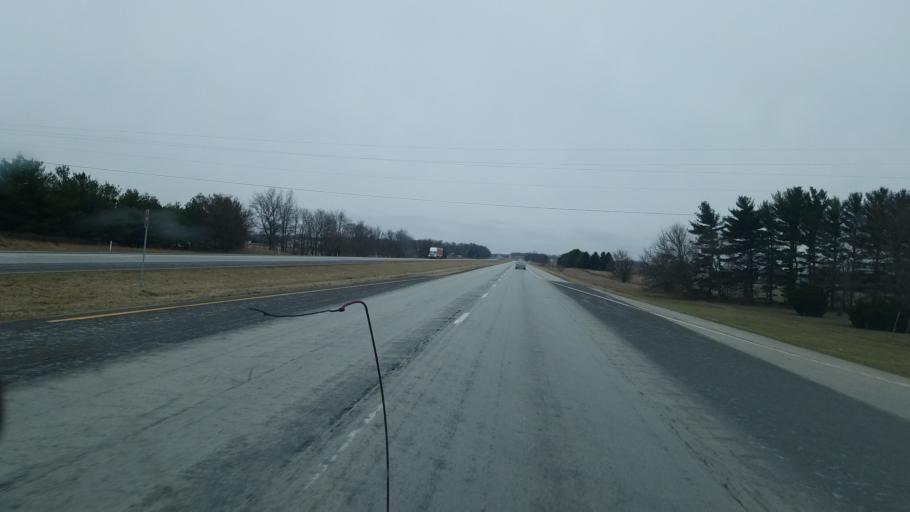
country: US
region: Indiana
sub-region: Fulton County
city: Rochester
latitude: 41.0687
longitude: -86.2401
